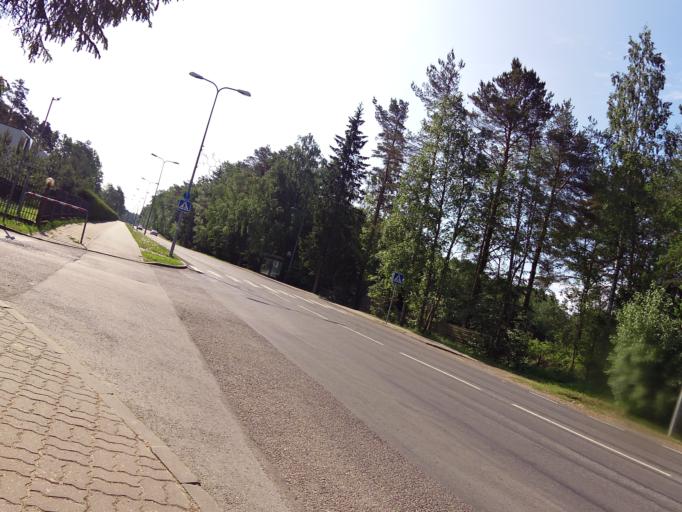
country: EE
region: Harju
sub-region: Harku vald
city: Tabasalu
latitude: 59.4451
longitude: 24.6119
